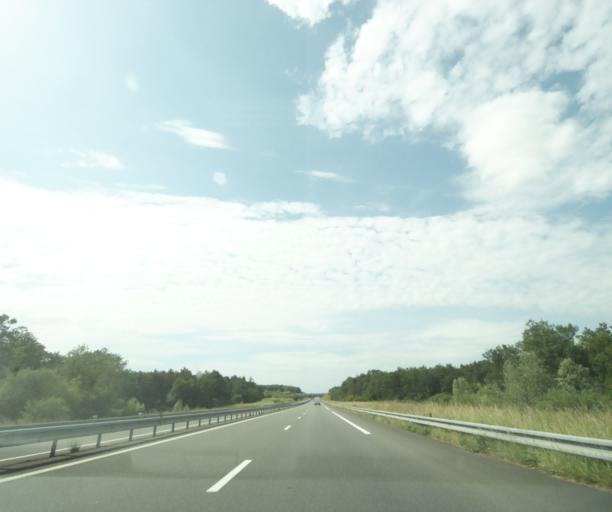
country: FR
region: Pays de la Loire
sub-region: Departement de Maine-et-Loire
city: Baune
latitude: 47.4976
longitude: -0.2786
